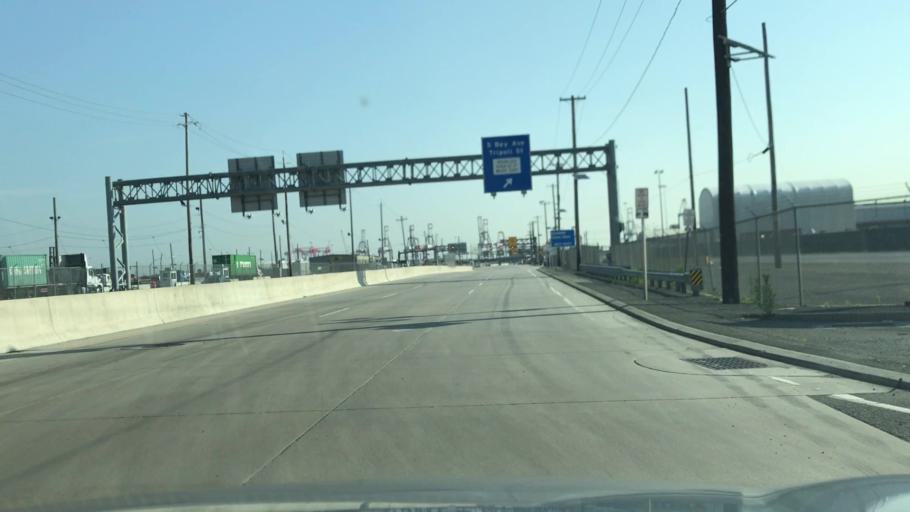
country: US
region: New Jersey
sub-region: Hudson County
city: Bayonne
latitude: 40.6709
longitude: -74.1623
